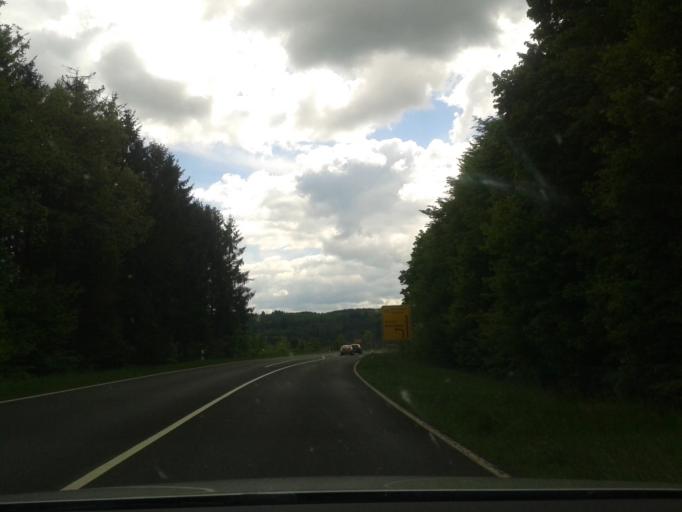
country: DE
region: Hesse
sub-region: Regierungsbezirk Giessen
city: Bischoffen
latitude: 50.7048
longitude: 8.4782
